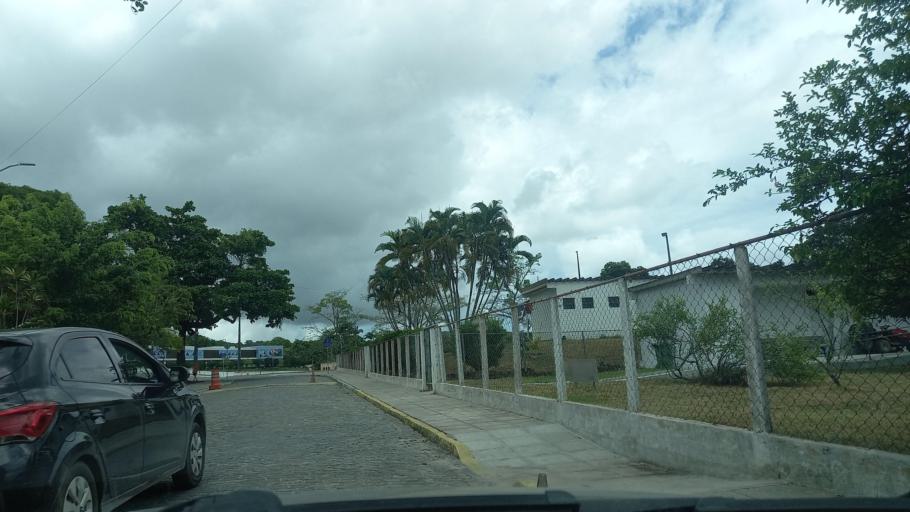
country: BR
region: Pernambuco
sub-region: Sao Lourenco Da Mata
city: Sao Lourenco da Mata
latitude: -8.0161
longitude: -34.9509
